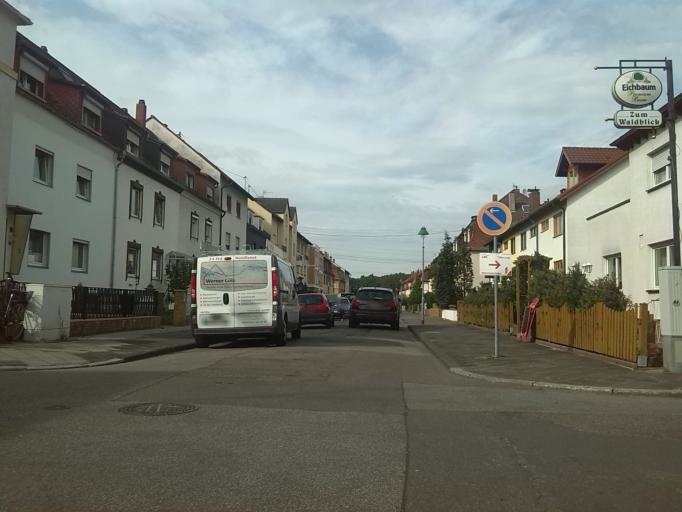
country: DE
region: Rheinland-Pfalz
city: Altrip
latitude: 49.4437
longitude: 8.5326
